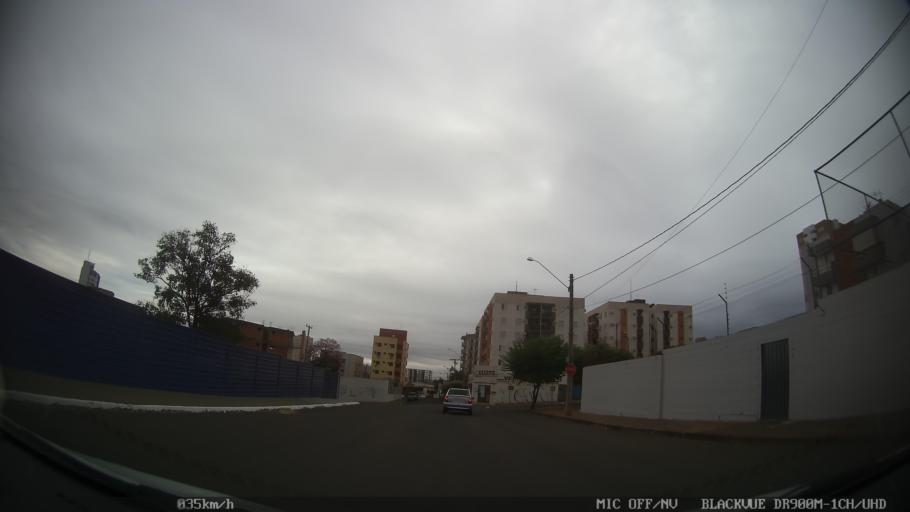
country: BR
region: Sao Paulo
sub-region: Sao Jose Do Rio Preto
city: Sao Jose do Rio Preto
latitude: -20.8315
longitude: -49.3894
